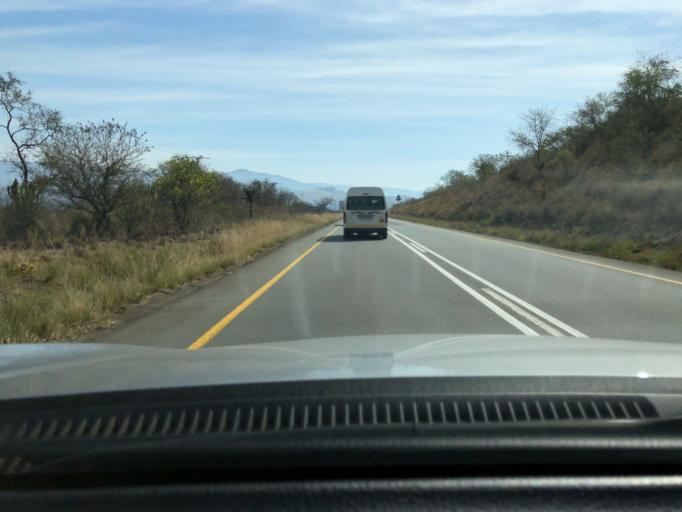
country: ZA
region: KwaZulu-Natal
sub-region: uMgungundlovu District Municipality
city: Richmond
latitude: -30.0317
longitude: 30.2214
